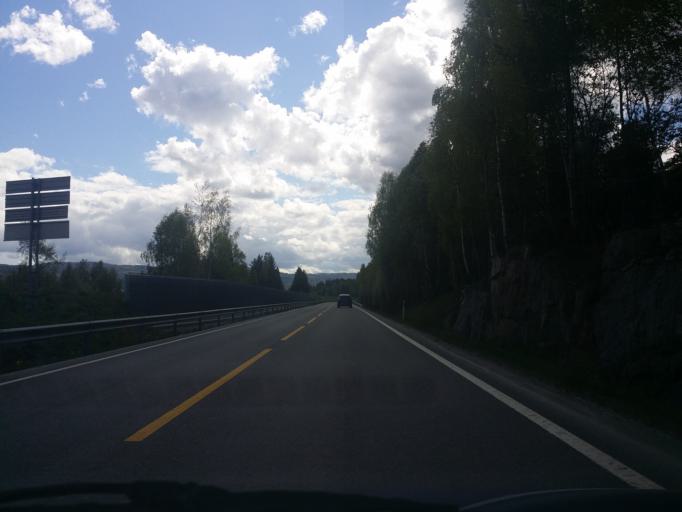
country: NO
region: Buskerud
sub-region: Modum
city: Vikersund
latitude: 59.9617
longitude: 9.9795
